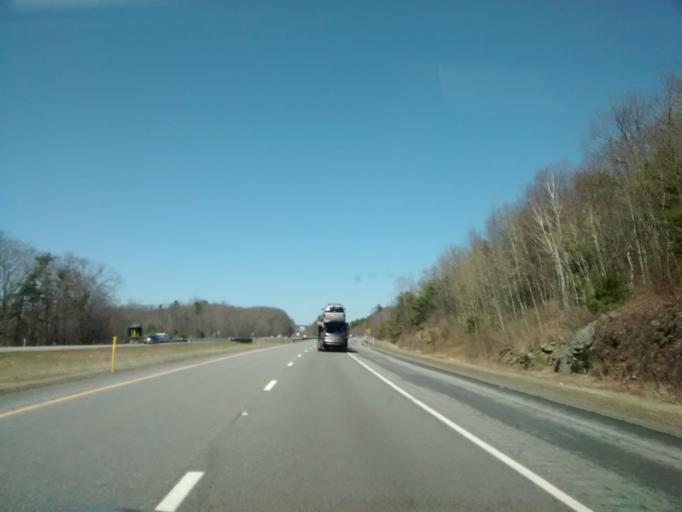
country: US
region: Massachusetts
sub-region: Worcester County
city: Oxford
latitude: 42.1293
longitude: -71.8574
